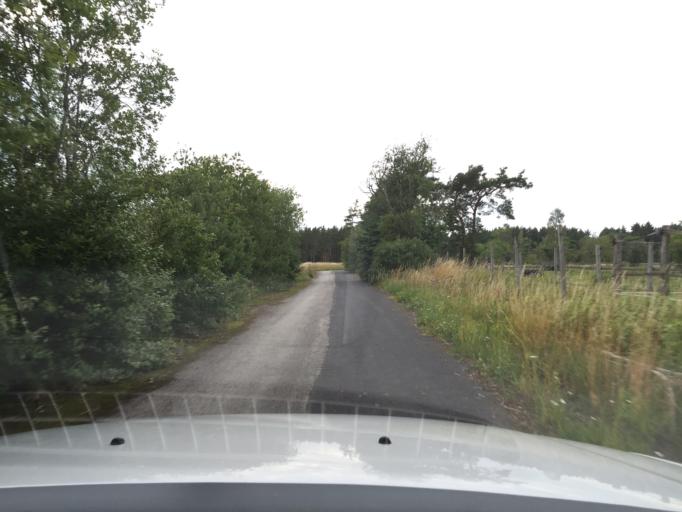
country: SE
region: Skane
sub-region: Kristianstads Kommun
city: Norra Asum
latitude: 55.9394
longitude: 14.0723
